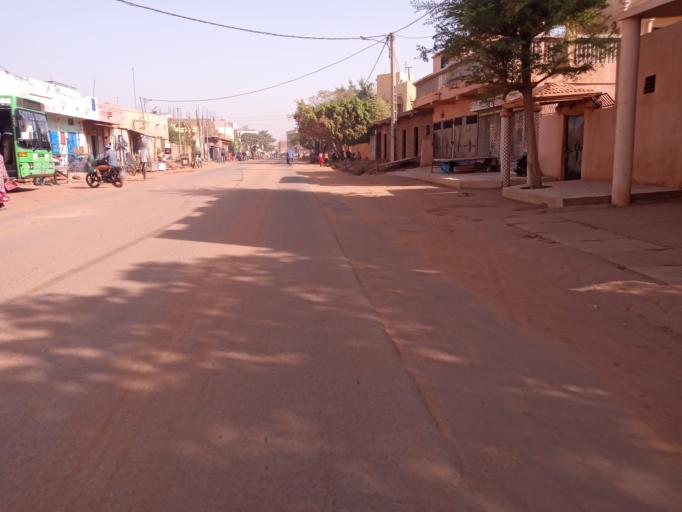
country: ML
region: Bamako
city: Bamako
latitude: 12.5810
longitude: -7.9578
